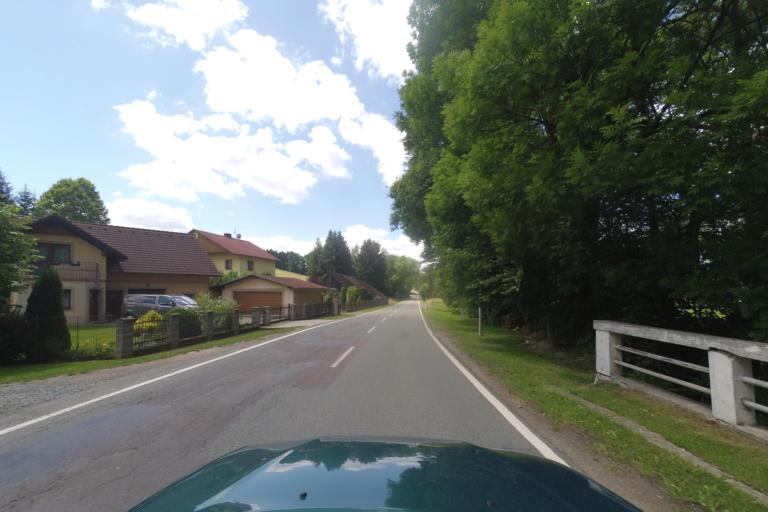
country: CZ
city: Dobruska
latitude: 50.3239
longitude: 16.2094
